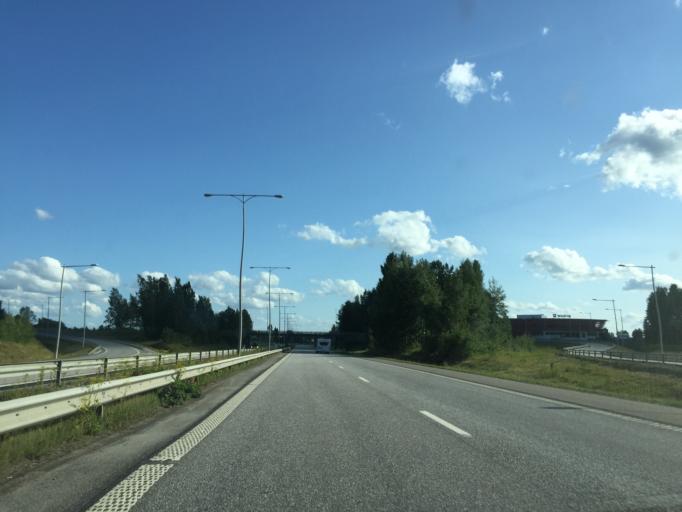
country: SE
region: OErebro
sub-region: Orebro Kommun
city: Orebro
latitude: 59.2416
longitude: 15.1457
